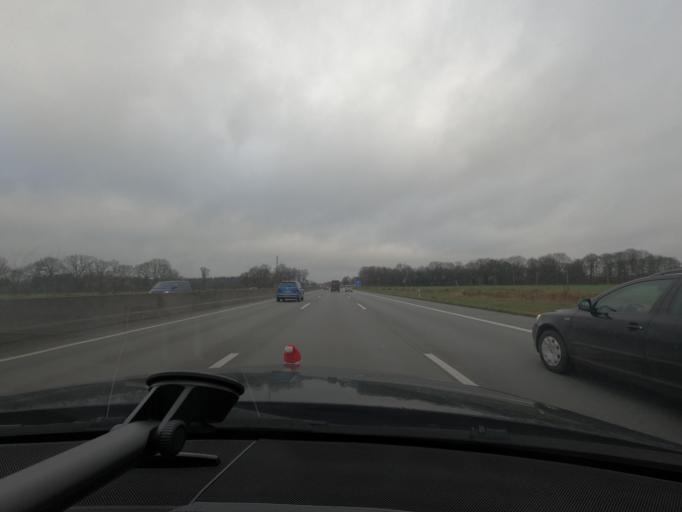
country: DE
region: Schleswig-Holstein
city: Bonningstedt
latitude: 53.6644
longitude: 9.9361
